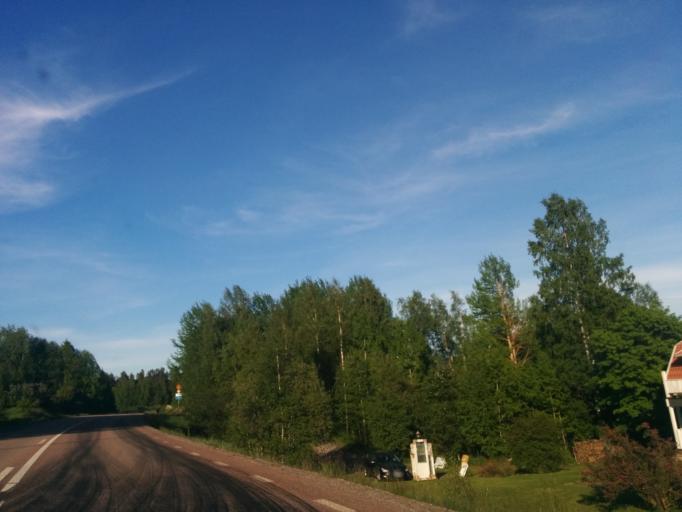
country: SE
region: Vaesternorrland
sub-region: Kramfors Kommun
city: Kramfors
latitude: 63.0229
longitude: 17.7644
